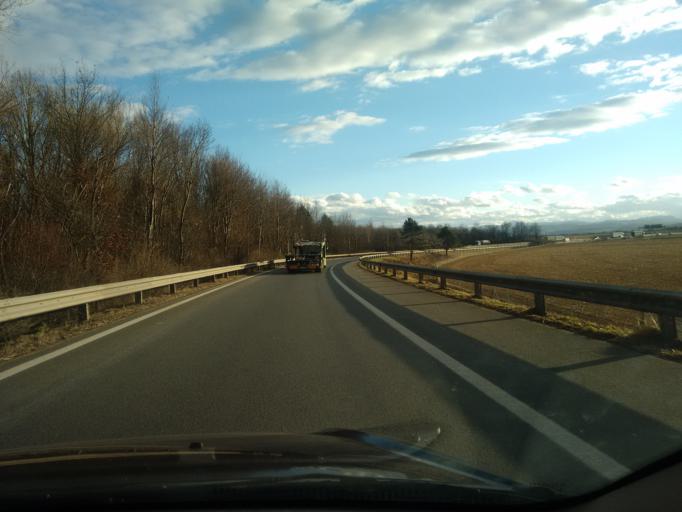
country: AT
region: Lower Austria
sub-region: Politischer Bezirk Sankt Polten
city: Pyhra
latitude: 48.1815
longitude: 15.6615
